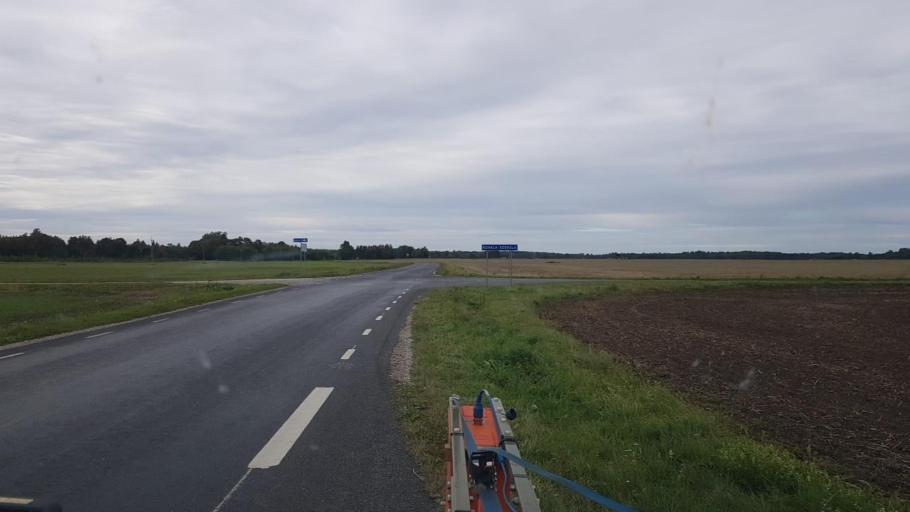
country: EE
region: Laeaene-Virumaa
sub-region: Viru-Nigula vald
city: Kunda
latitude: 59.4061
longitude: 26.5194
